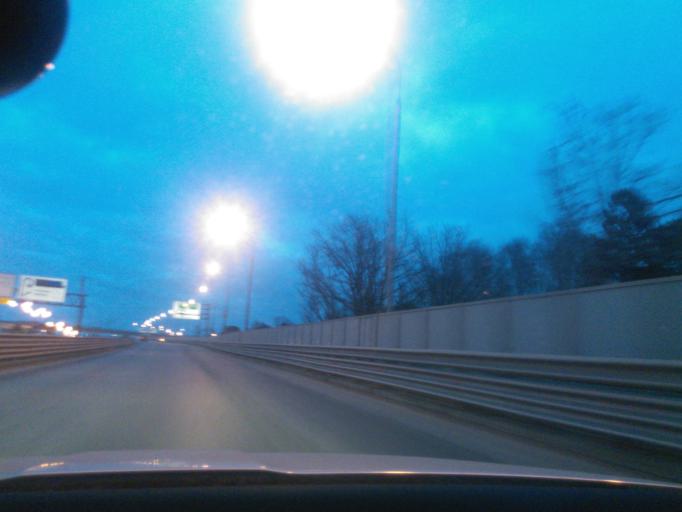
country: RU
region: Moskovskaya
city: Levoberezhnaya
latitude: 55.8838
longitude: 37.4708
